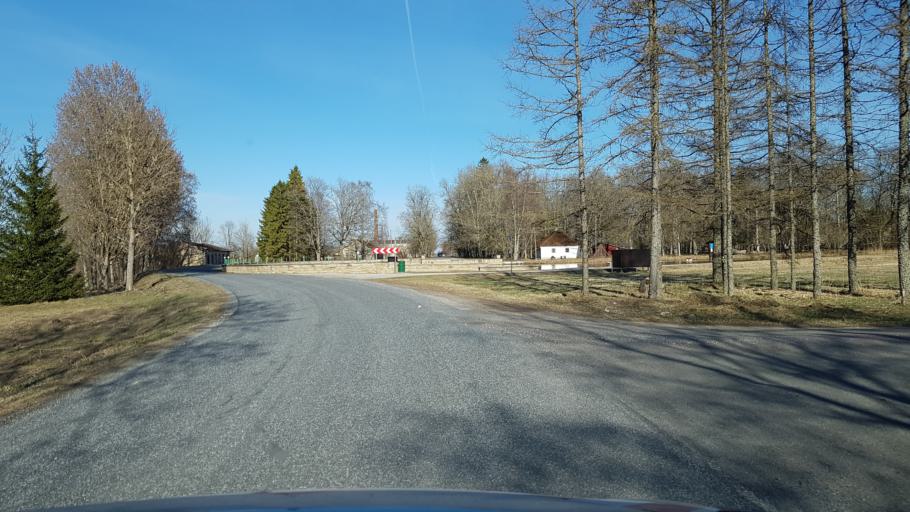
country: EE
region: Laeaene-Virumaa
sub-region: Vinni vald
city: Vinni
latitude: 59.1721
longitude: 26.5946
